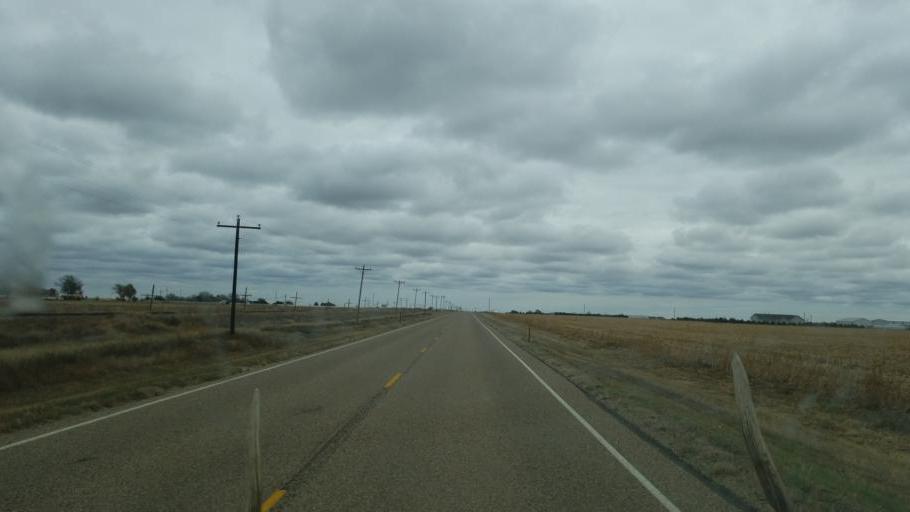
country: US
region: Colorado
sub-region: Kiowa County
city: Eads
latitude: 38.4849
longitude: -102.8464
